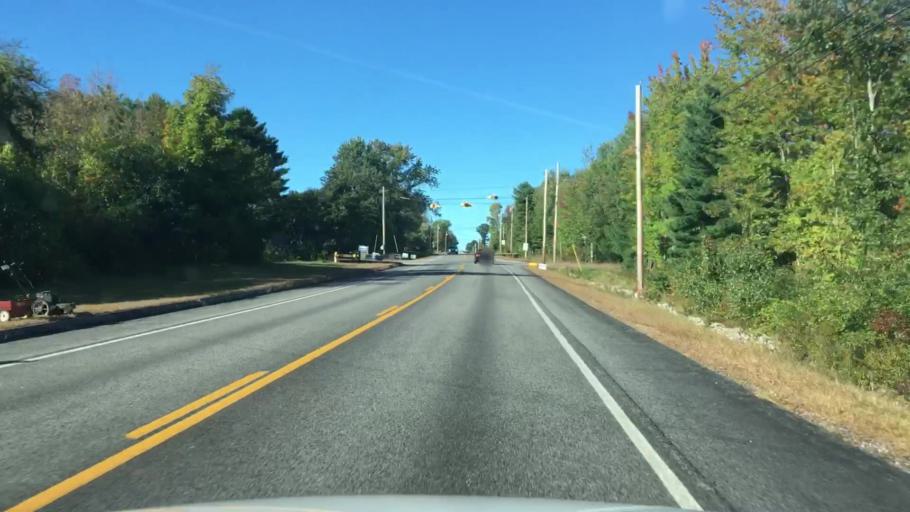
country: US
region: Maine
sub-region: Androscoggin County
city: Lisbon Falls
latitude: 44.0235
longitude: -70.0672
